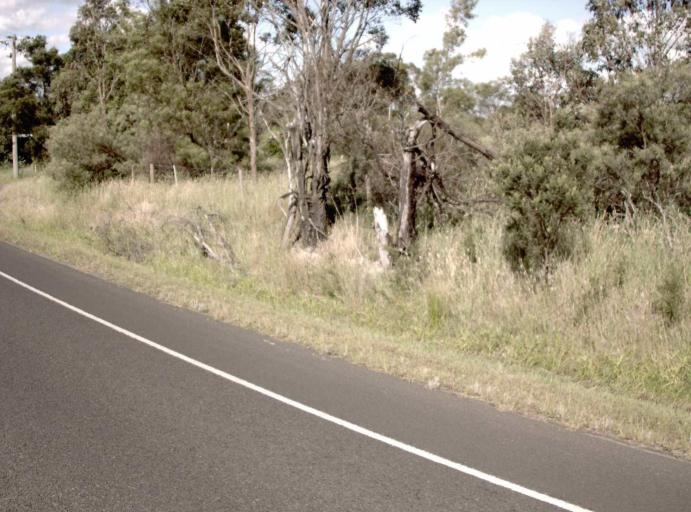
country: AU
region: Victoria
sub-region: Latrobe
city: Morwell
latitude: -38.1718
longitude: 146.4067
